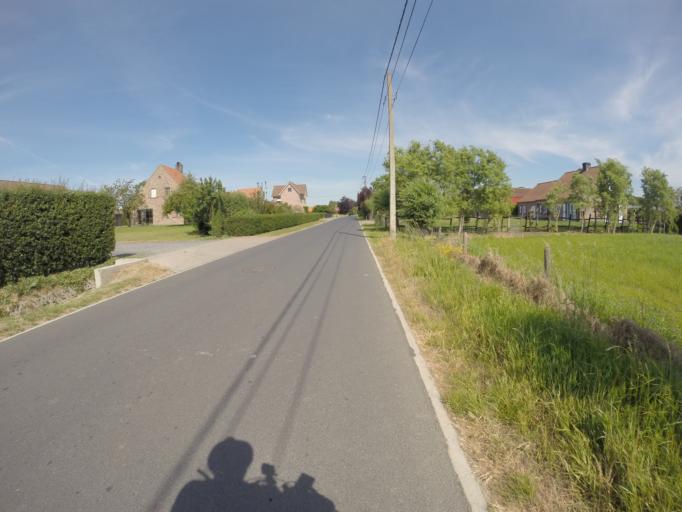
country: BE
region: Flanders
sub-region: Provincie Oost-Vlaanderen
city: Knesselare
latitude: 51.1716
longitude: 3.3832
